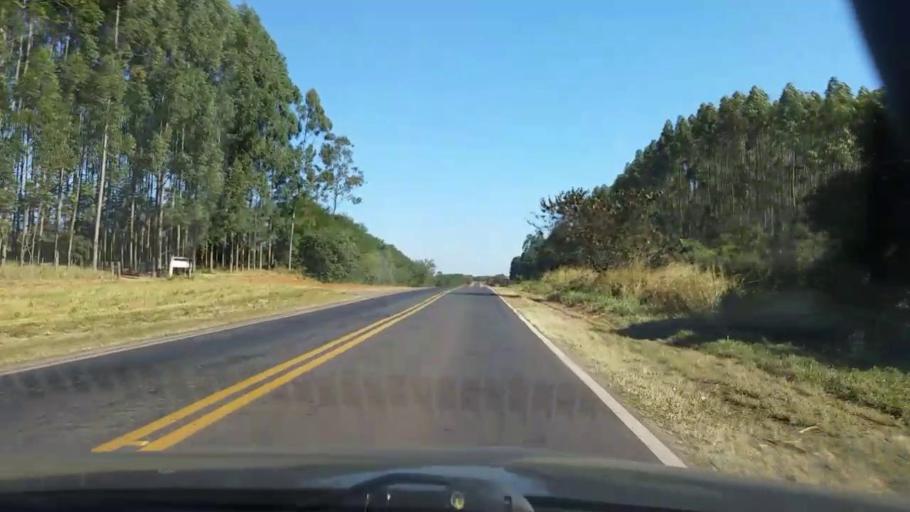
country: BR
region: Sao Paulo
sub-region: Avare
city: Avare
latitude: -22.9222
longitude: -48.7851
